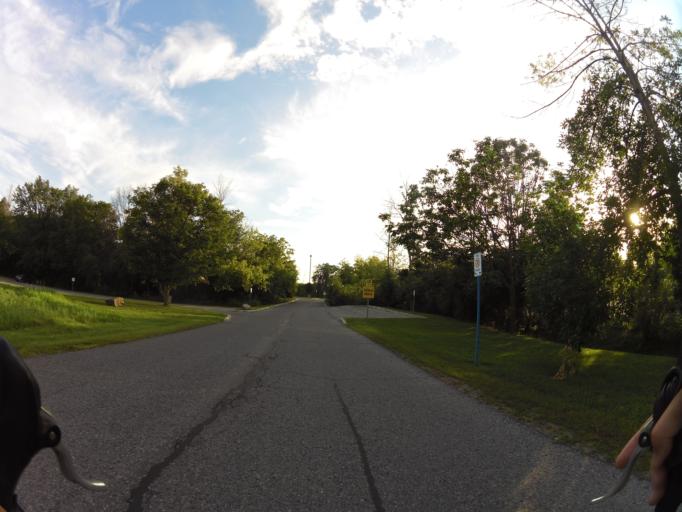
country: CA
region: Ontario
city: Bells Corners
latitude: 45.3427
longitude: -75.9227
